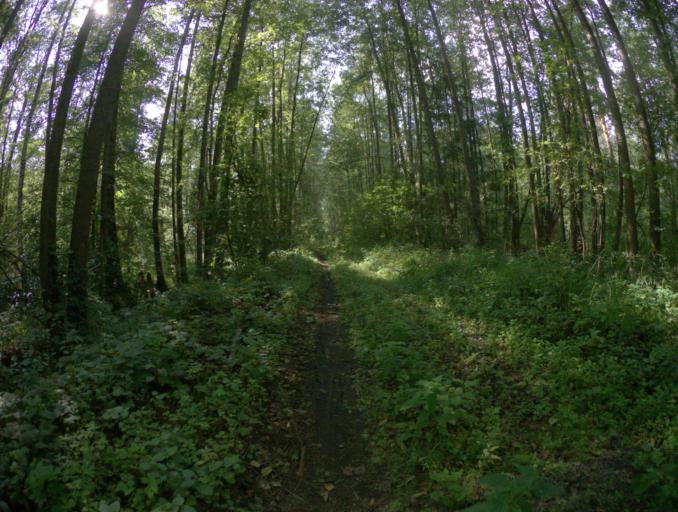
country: RU
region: Vladimir
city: Sobinka
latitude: 55.9092
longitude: 40.1261
